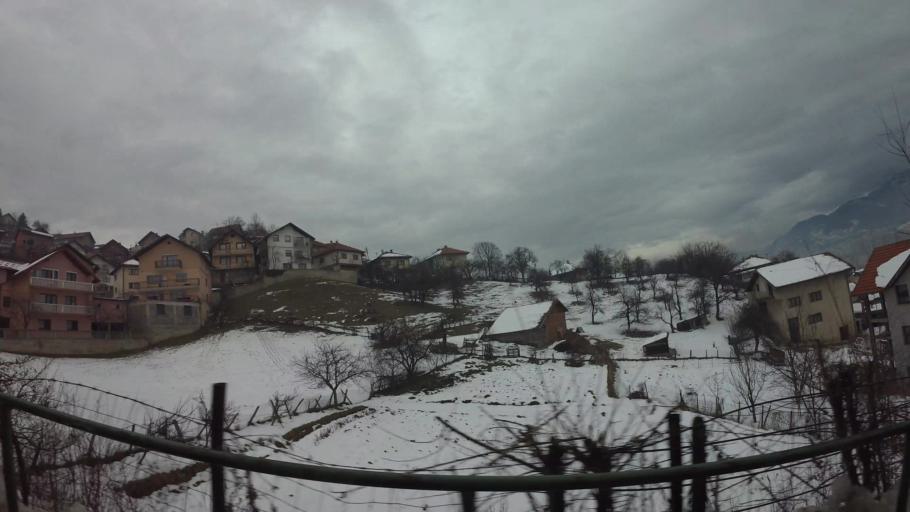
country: BA
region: Federation of Bosnia and Herzegovina
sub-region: Kanton Sarajevo
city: Sarajevo
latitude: 43.8542
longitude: 18.3591
